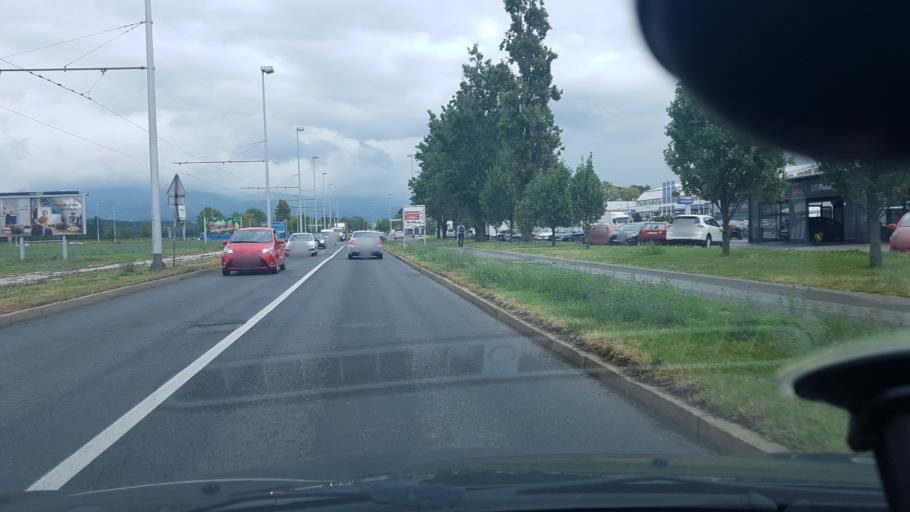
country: HR
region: Grad Zagreb
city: Dubrava
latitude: 45.8217
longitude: 16.0369
